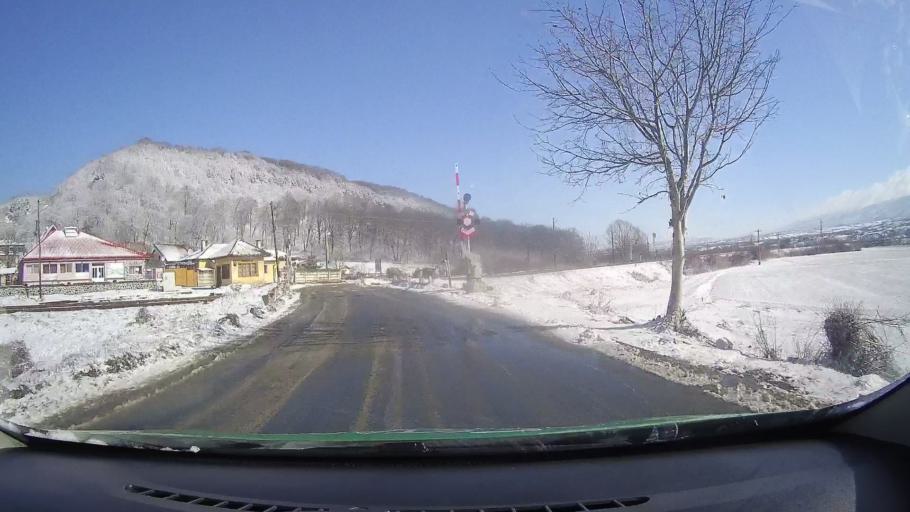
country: RO
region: Sibiu
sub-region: Comuna Turnu Rosu
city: Turnu Rosu
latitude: 45.6618
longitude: 24.3003
